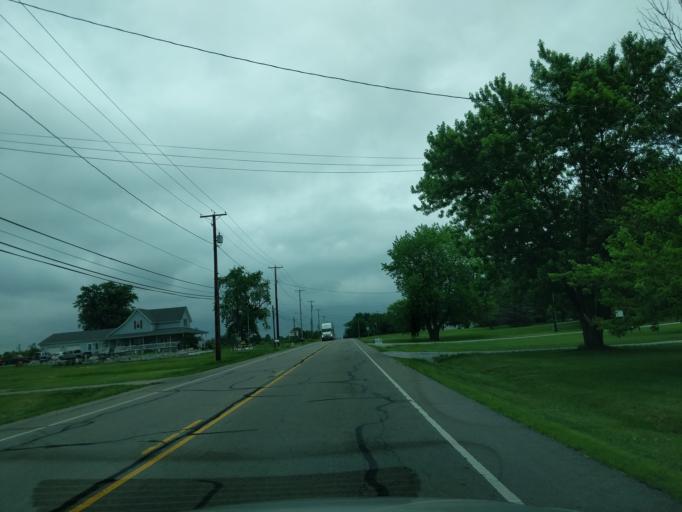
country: US
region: Indiana
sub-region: Madison County
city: Alexandria
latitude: 40.2778
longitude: -85.6603
